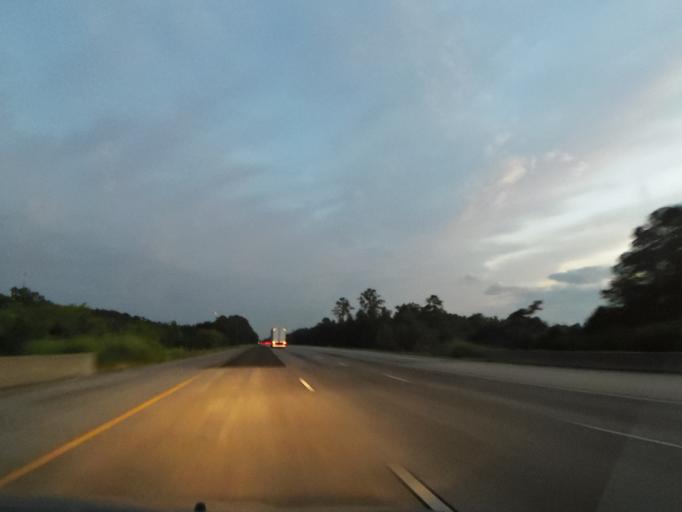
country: US
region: Georgia
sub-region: Liberty County
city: Midway
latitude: 31.7165
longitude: -81.3901
